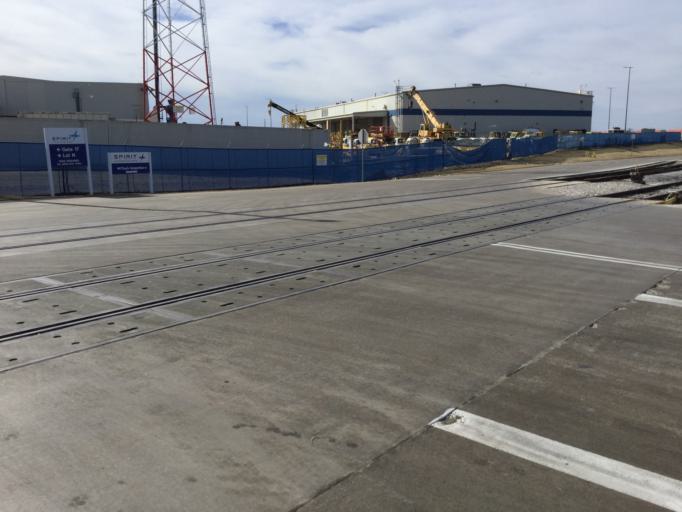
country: US
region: Kansas
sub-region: Sedgwick County
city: Derby
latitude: 37.6240
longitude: -97.2910
